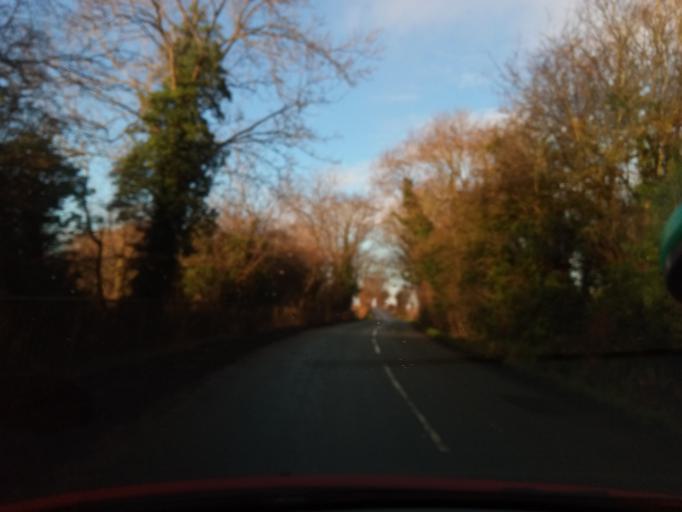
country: GB
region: England
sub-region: Derbyshire
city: Melbourne
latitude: 52.8515
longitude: -1.4285
